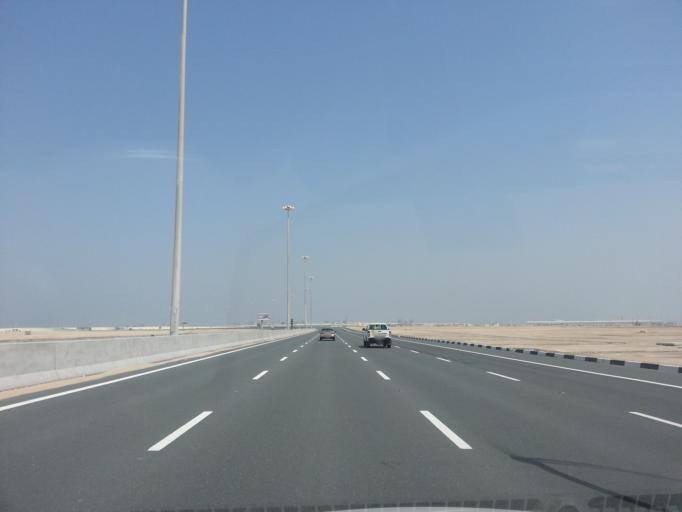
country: AE
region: Abu Dhabi
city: Abu Dhabi
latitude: 24.7546
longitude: 54.7343
